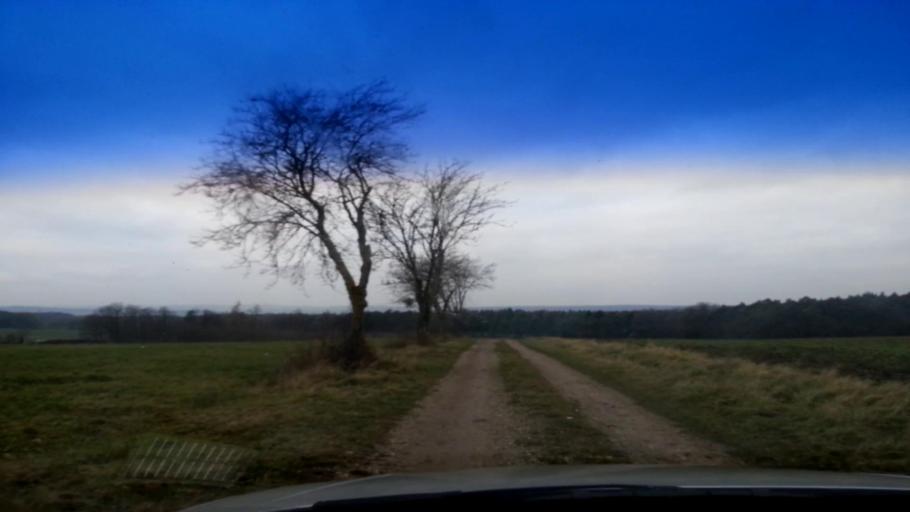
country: DE
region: Bavaria
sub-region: Upper Franconia
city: Pommersfelden
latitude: 49.8028
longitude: 10.7860
